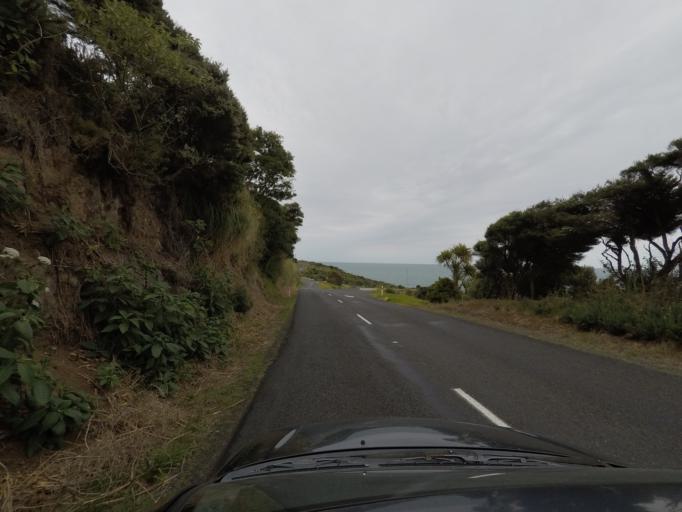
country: NZ
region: Waikato
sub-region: Waikato District
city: Raglan
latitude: -37.8231
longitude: 174.8127
